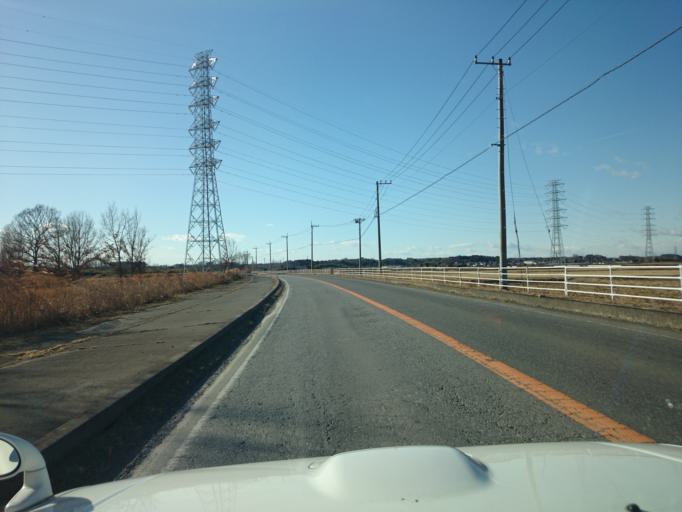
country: JP
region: Ibaraki
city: Tsukuba
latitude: 36.1453
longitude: 140.1101
